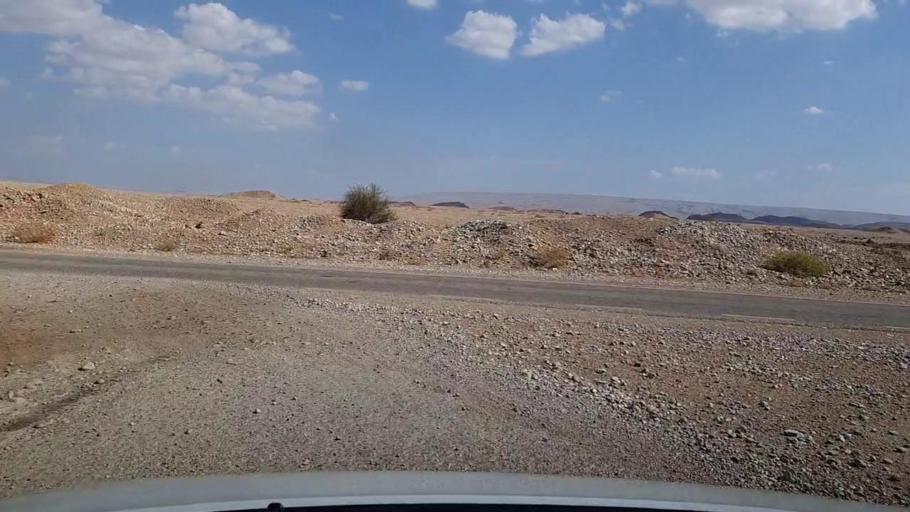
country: PK
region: Sindh
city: Bhan
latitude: 26.3640
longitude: 67.6400
